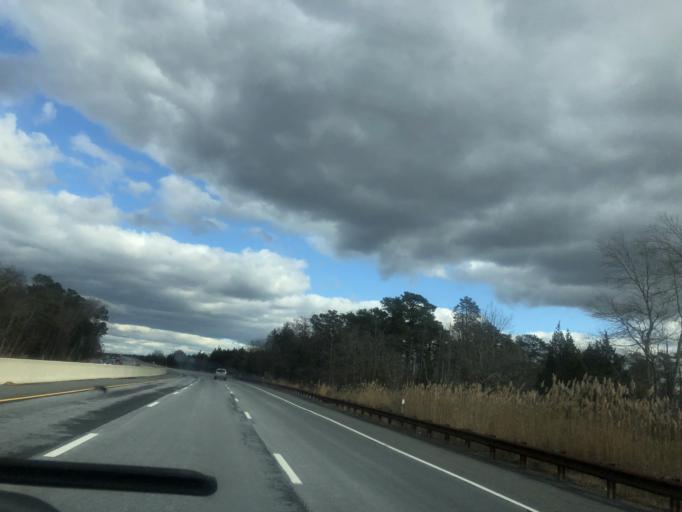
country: US
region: New Jersey
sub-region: Atlantic County
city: Port Republic
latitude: 39.5854
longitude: -74.4525
